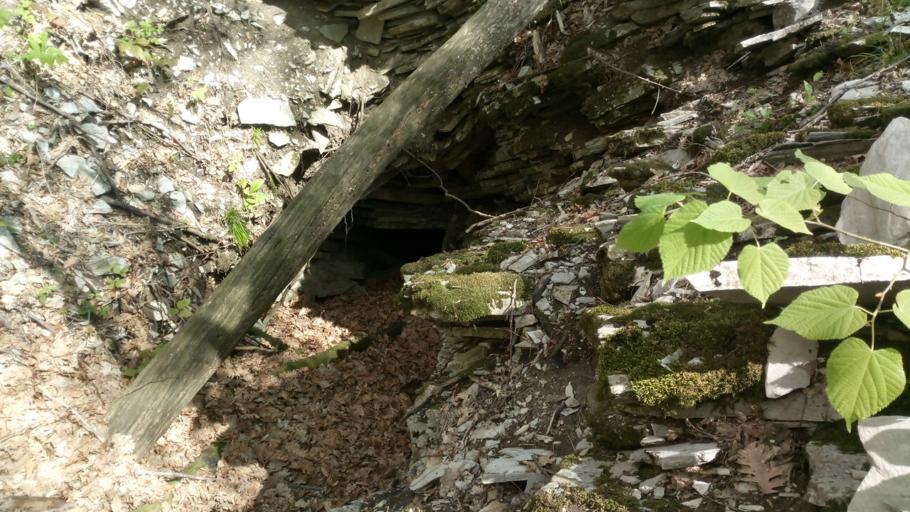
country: RU
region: Krasnodarskiy
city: Novomikhaylovskiy
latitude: 44.3634
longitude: 38.8798
